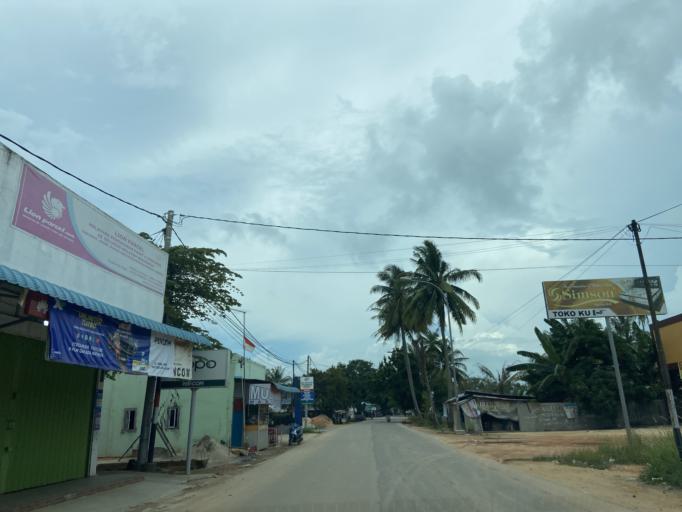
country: SG
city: Singapore
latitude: 1.1511
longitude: 104.1333
